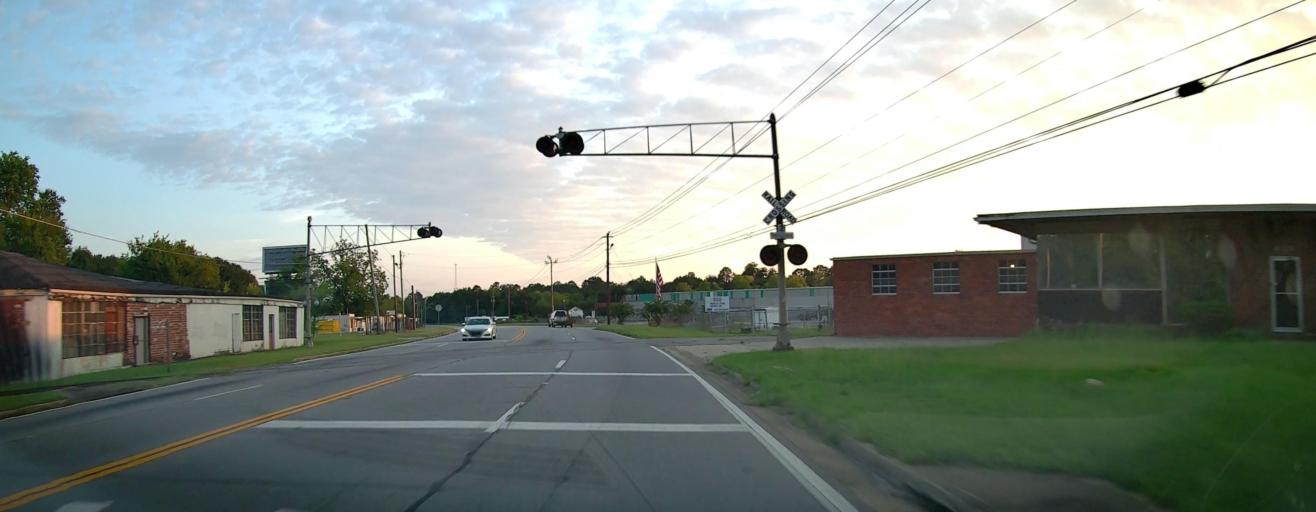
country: US
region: Georgia
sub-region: Bibb County
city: Macon
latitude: 32.7926
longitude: -83.6497
